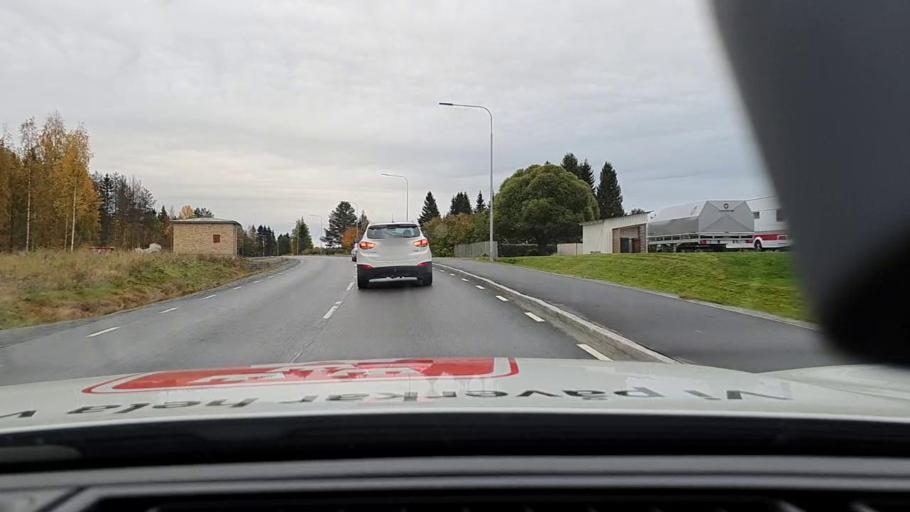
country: SE
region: Norrbotten
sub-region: Bodens Kommun
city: Saevast
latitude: 65.7752
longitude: 21.6948
